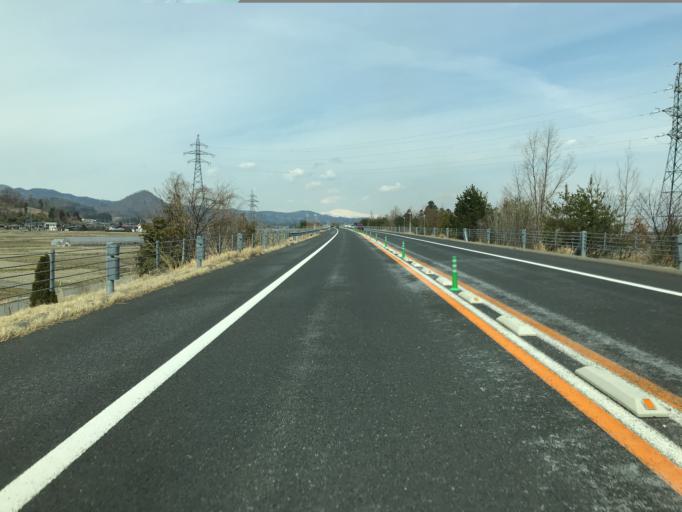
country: JP
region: Yamagata
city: Kaminoyama
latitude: 38.2109
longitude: 140.2915
